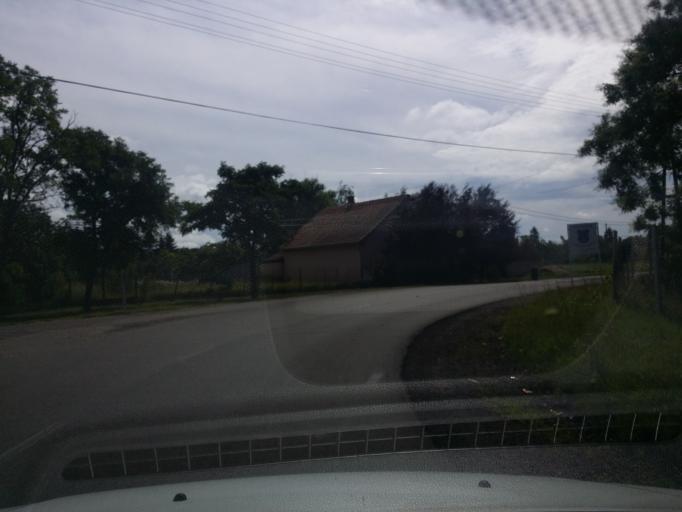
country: HU
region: Heves
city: Besenyotelek
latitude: 47.6031
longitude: 20.4299
